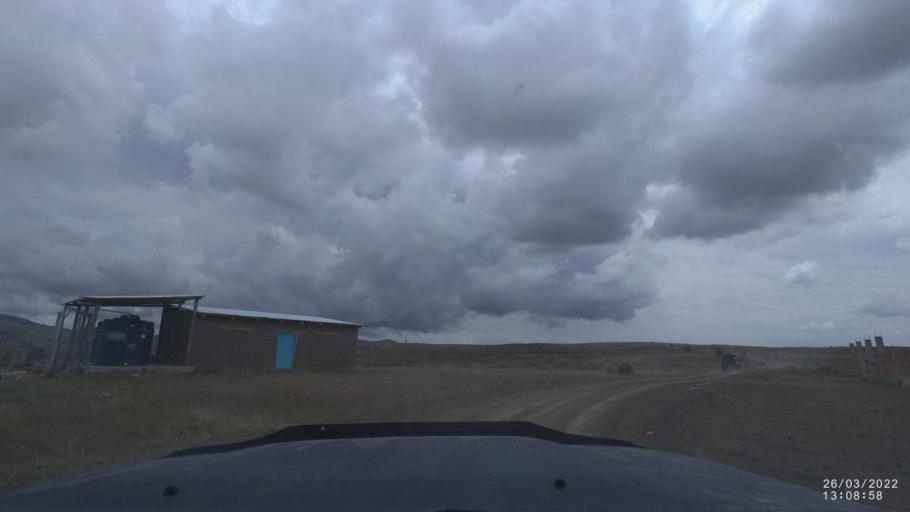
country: BO
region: Cochabamba
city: Cliza
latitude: -17.7381
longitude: -65.8508
